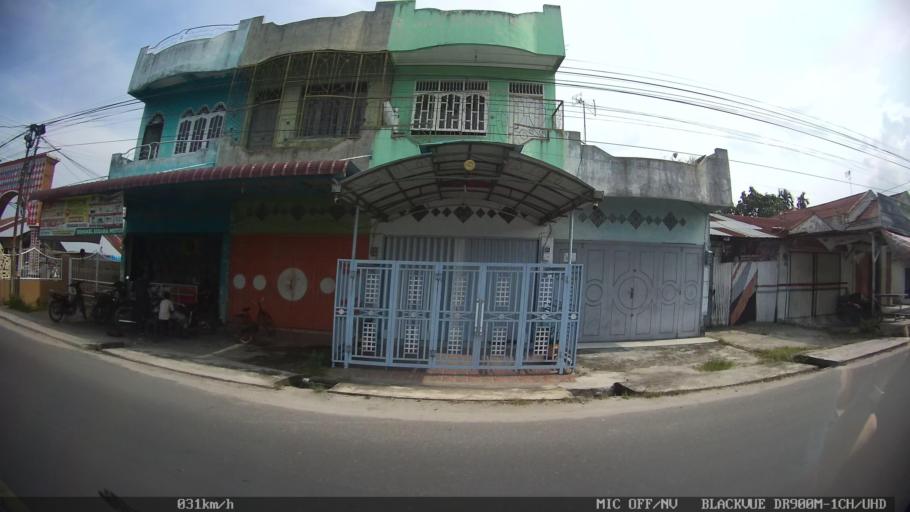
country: ID
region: North Sumatra
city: Percut
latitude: 3.6070
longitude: 98.7934
